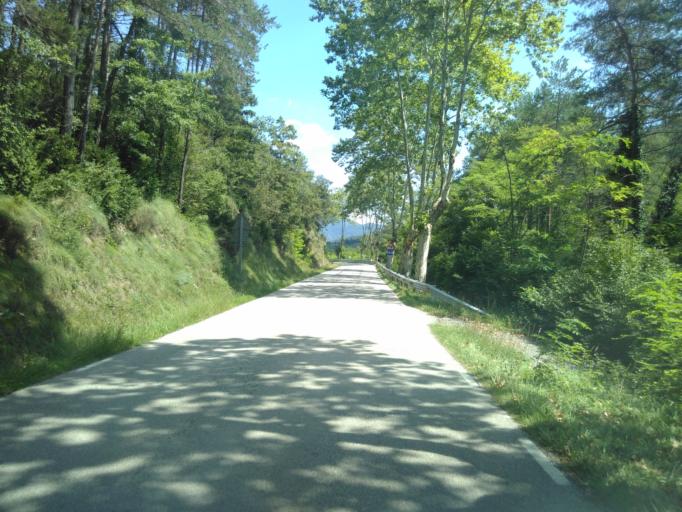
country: ES
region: Catalonia
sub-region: Provincia de Barcelona
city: Sora
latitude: 42.0961
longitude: 2.1899
